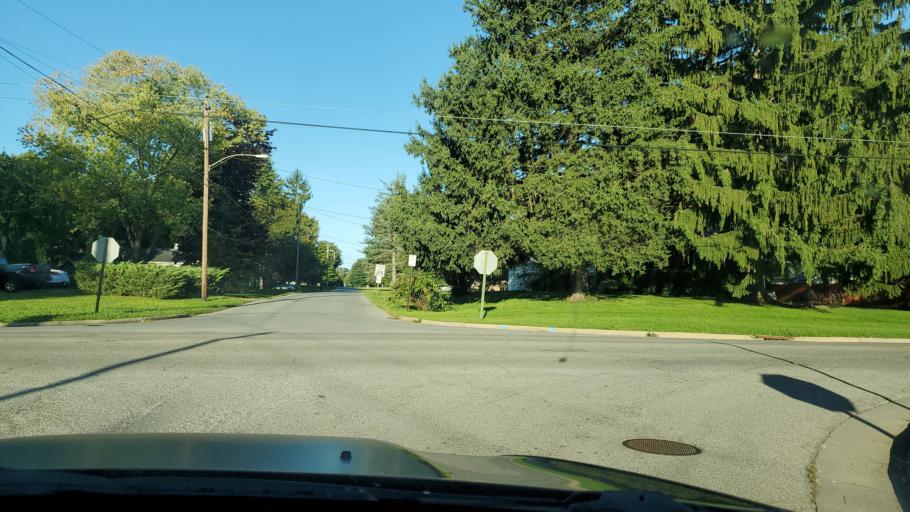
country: US
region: Ohio
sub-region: Mahoning County
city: Struthers
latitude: 41.0466
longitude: -80.6213
